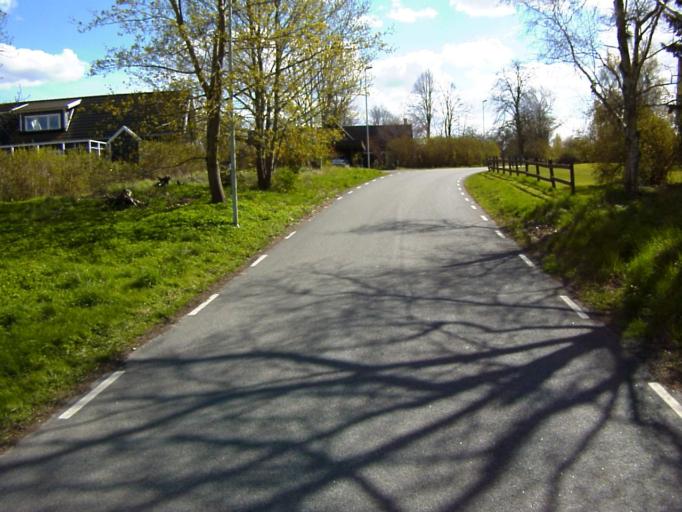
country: SE
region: Skane
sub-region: Kristianstads Kommun
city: Kristianstad
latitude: 56.0119
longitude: 14.0909
